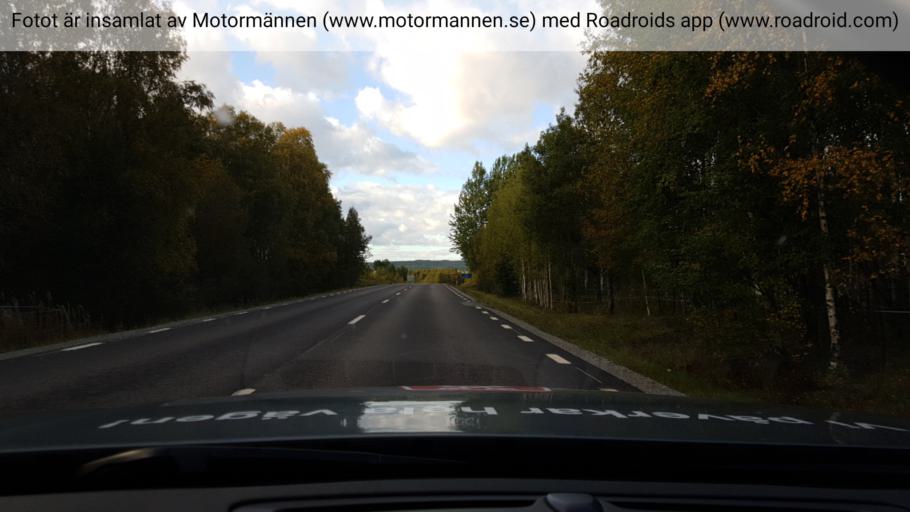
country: SE
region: Vaermland
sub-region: Filipstads Kommun
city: Filipstad
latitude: 59.8333
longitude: 14.0977
